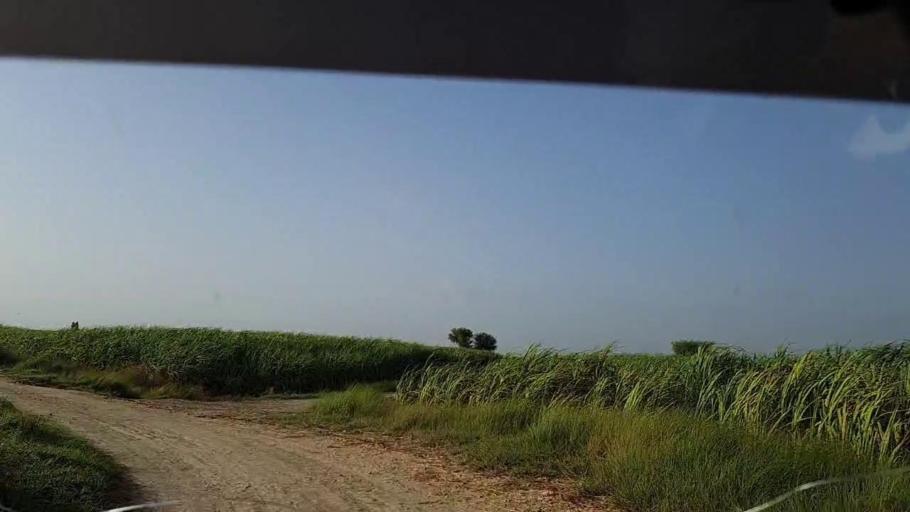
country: PK
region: Sindh
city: Badin
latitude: 24.5664
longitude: 68.8826
